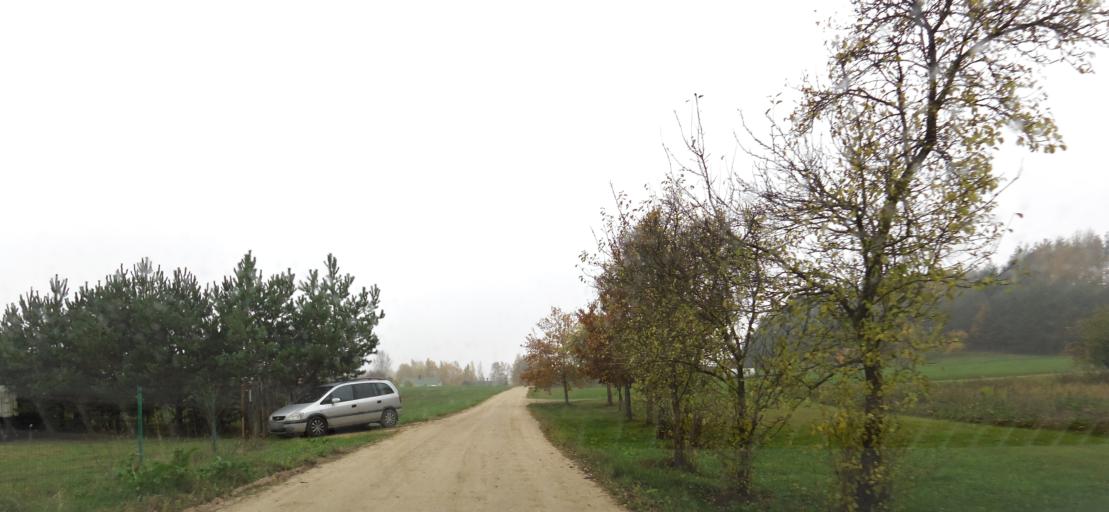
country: LT
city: Skaidiskes
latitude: 54.6215
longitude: 25.4722
